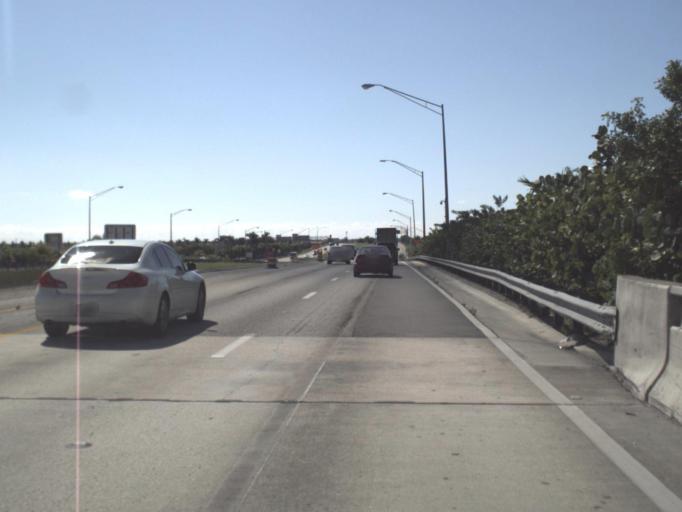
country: US
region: Florida
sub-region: Miami-Dade County
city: Goulds
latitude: 25.5663
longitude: -80.3632
